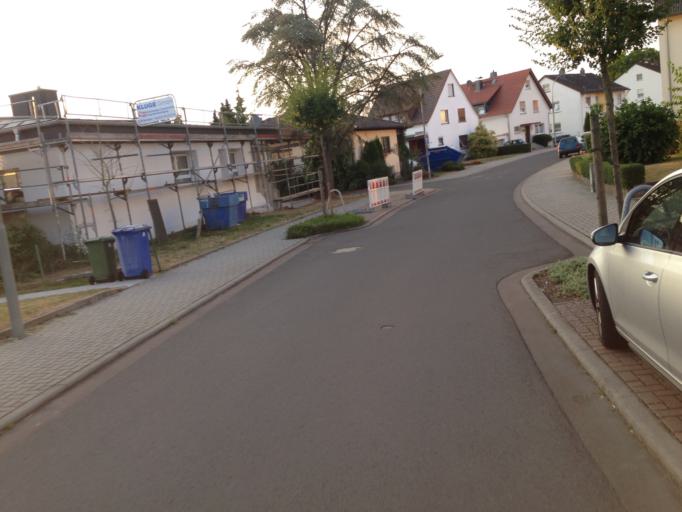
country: DE
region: Hesse
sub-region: Regierungsbezirk Giessen
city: Hoernsheim
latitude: 50.5251
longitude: 8.6493
